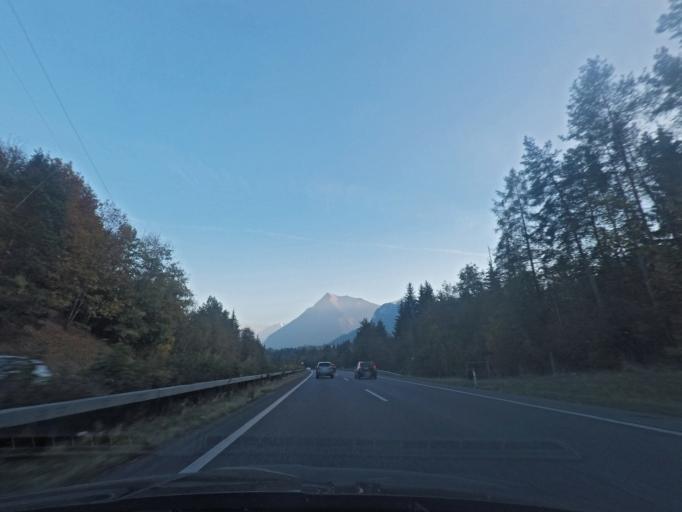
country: CH
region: Bern
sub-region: Thun District
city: Thun
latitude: 46.7220
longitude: 7.6086
